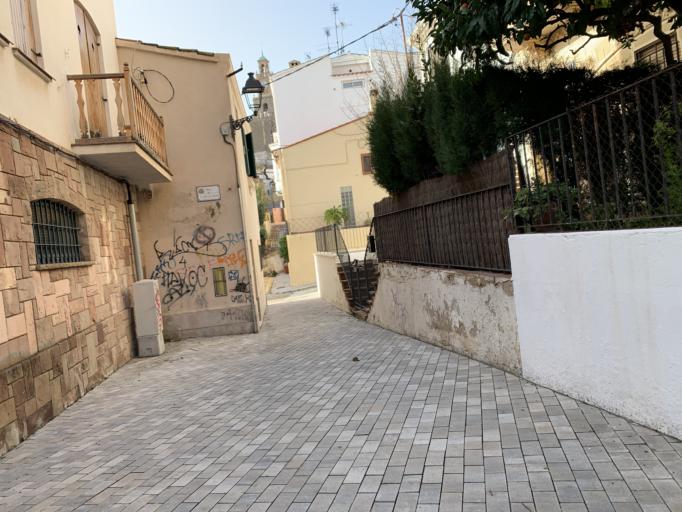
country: ES
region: Catalonia
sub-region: Provincia de Barcelona
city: El Masnou
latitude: 41.4801
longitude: 2.3177
